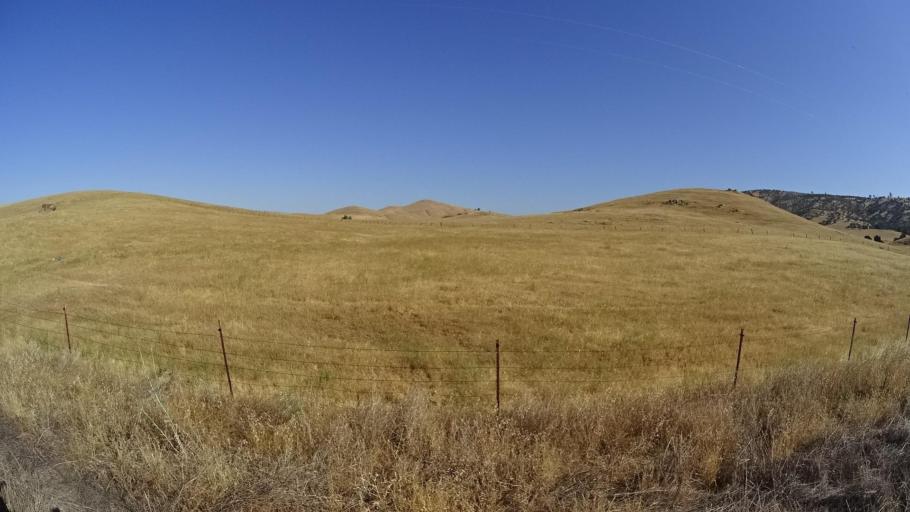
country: US
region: California
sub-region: Mariposa County
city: Mariposa
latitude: 37.5453
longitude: -120.1903
